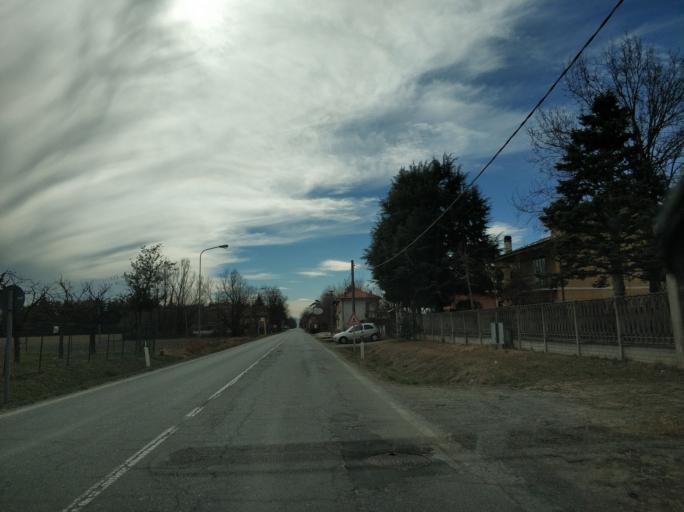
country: IT
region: Piedmont
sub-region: Provincia di Torino
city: Lombardore
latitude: 45.2262
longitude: 7.7316
